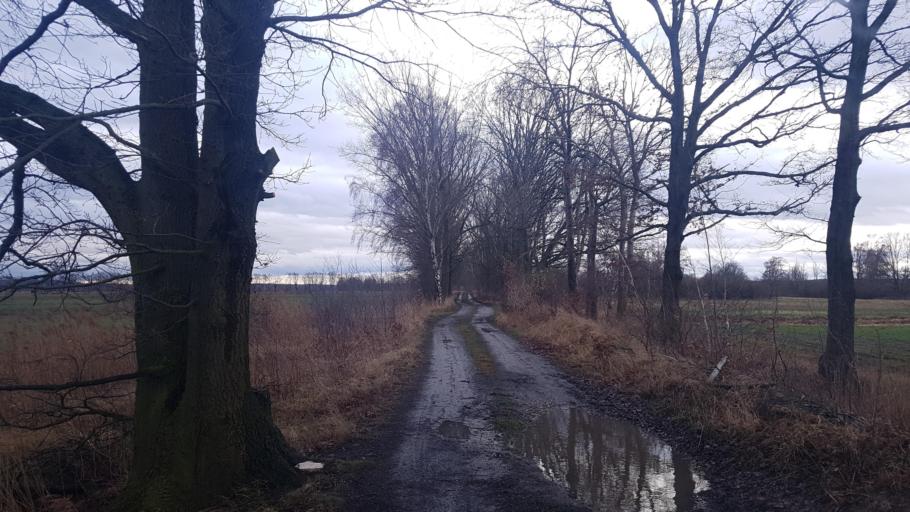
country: DE
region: Brandenburg
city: Plessa
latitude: 51.4336
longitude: 13.6499
